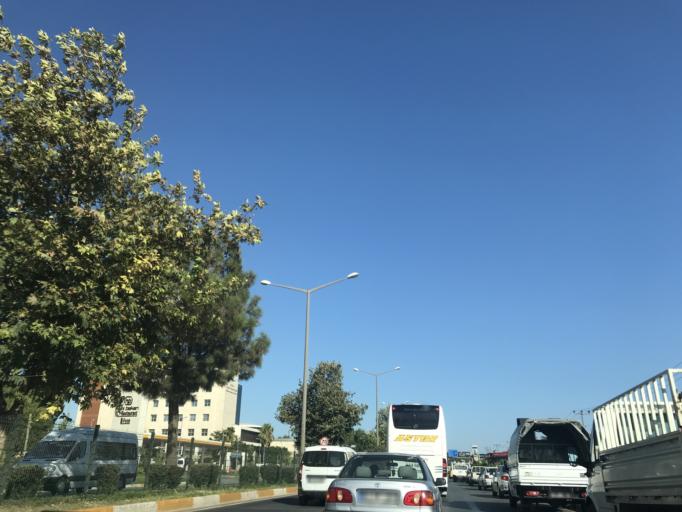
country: TR
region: Antalya
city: Antalya
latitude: 36.9027
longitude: 30.7573
